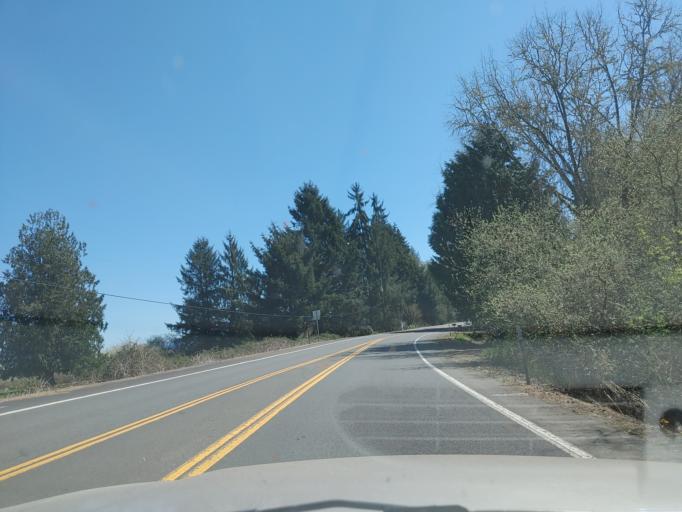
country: US
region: Oregon
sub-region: Clatsop County
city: Warrenton
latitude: 46.1532
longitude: -123.9033
